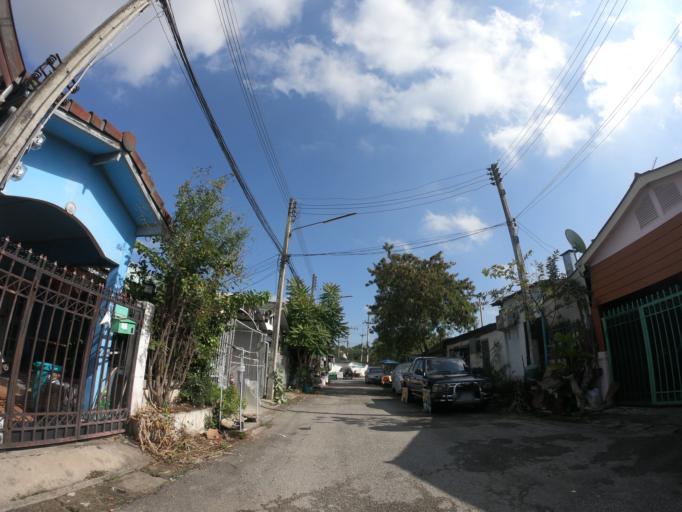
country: TH
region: Chiang Mai
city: Chiang Mai
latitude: 18.7865
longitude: 99.0384
